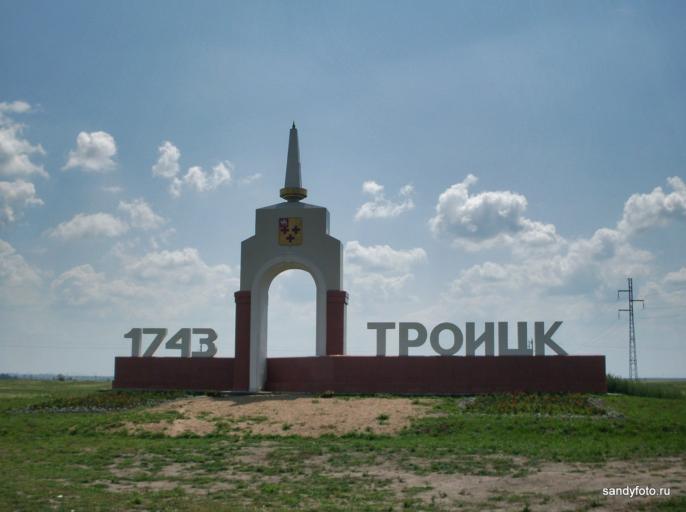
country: RU
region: Chelyabinsk
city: Troitsk
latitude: 54.0920
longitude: 61.4832
